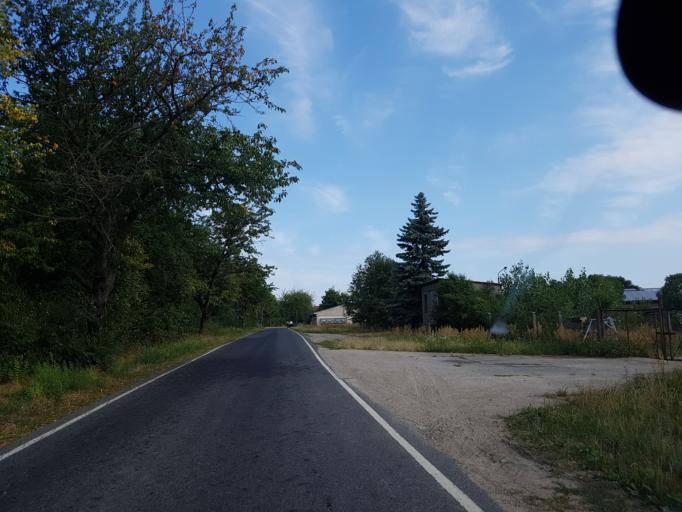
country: DE
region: Brandenburg
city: Drahnsdorf
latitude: 51.8501
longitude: 13.6217
